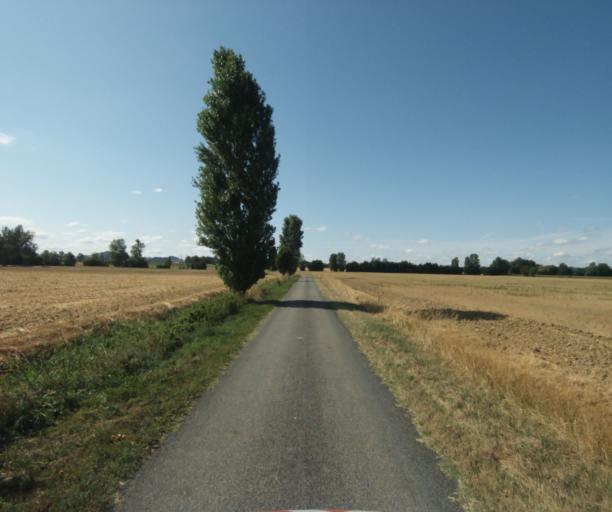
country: FR
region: Midi-Pyrenees
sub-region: Departement de la Haute-Garonne
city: Revel
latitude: 43.4952
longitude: 1.9862
